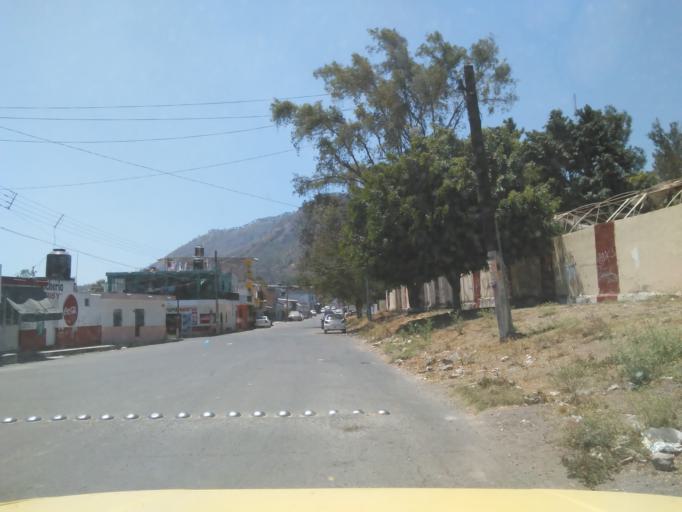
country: MX
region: Nayarit
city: Tepic
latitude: 21.5243
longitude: -104.9205
